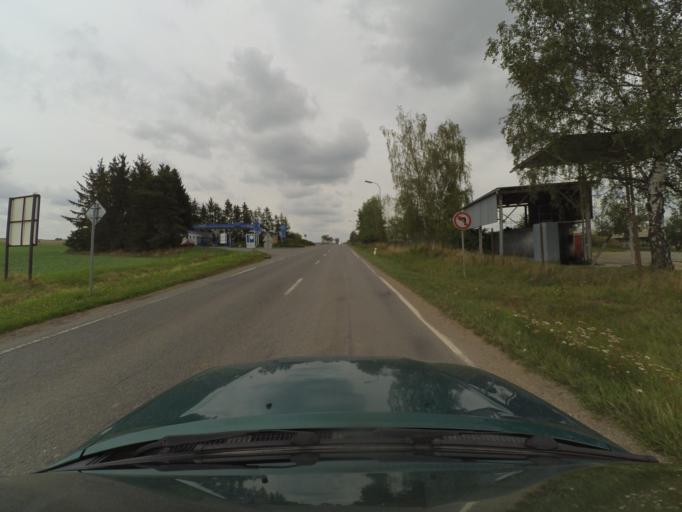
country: CZ
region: Plzensky
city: Kozlany
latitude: 50.0284
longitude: 13.5791
